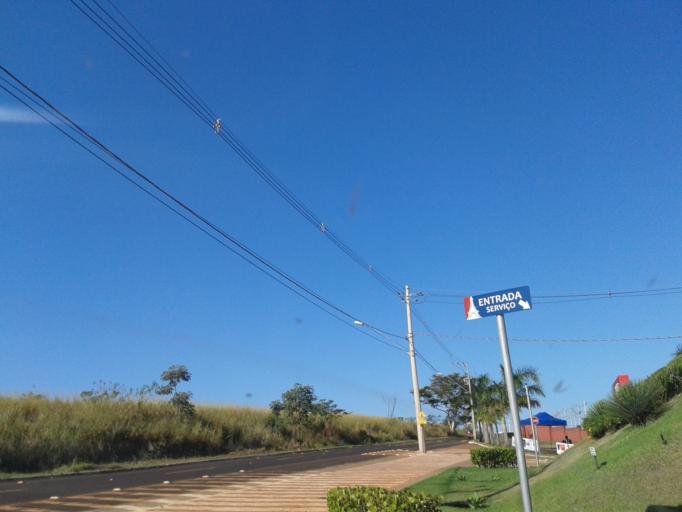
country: BR
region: Goias
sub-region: Itumbiara
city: Itumbiara
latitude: -18.4274
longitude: -49.2008
